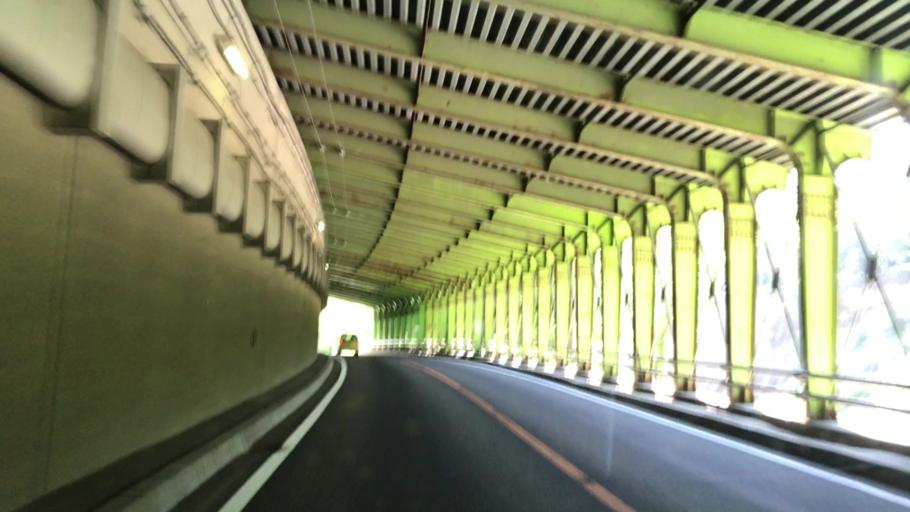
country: JP
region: Hokkaido
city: Shimo-furano
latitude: 42.9367
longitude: 142.5988
